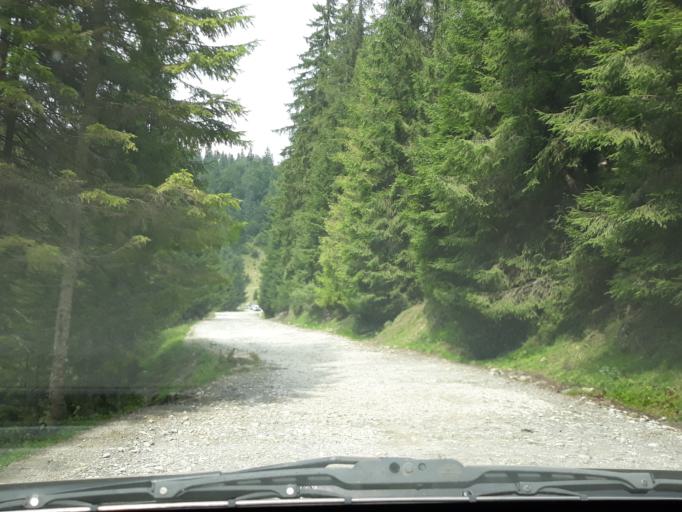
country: RO
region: Alba
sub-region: Comuna Arieseni
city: Arieseni
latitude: 46.5814
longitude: 22.7023
